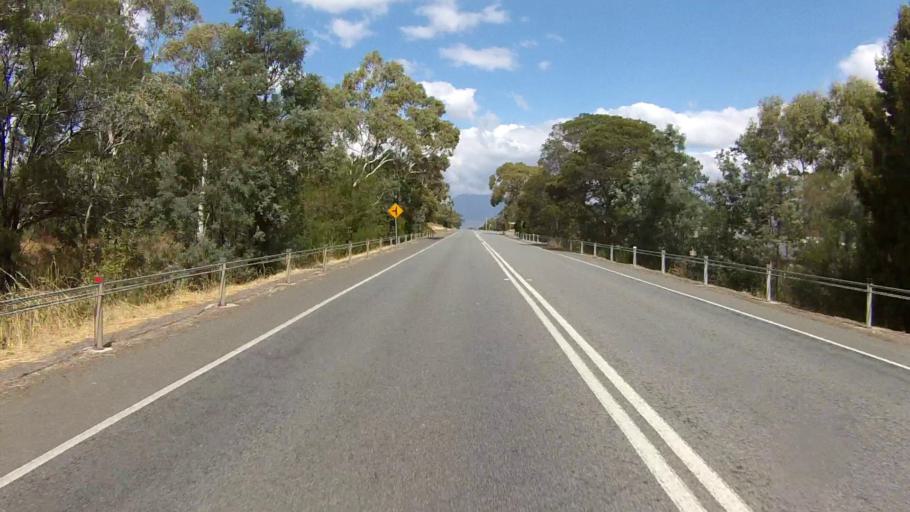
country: AU
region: Tasmania
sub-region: Brighton
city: Old Beach
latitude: -42.7684
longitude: 147.2697
